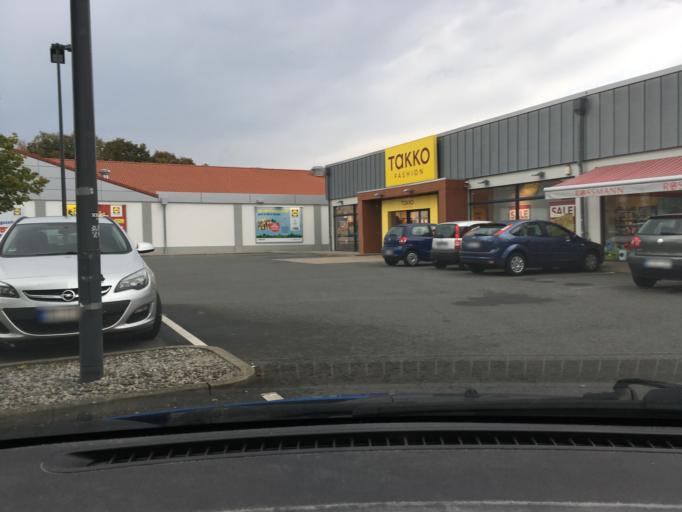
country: DE
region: Lower Saxony
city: Bad Munder am Deister
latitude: 52.1939
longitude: 9.4653
